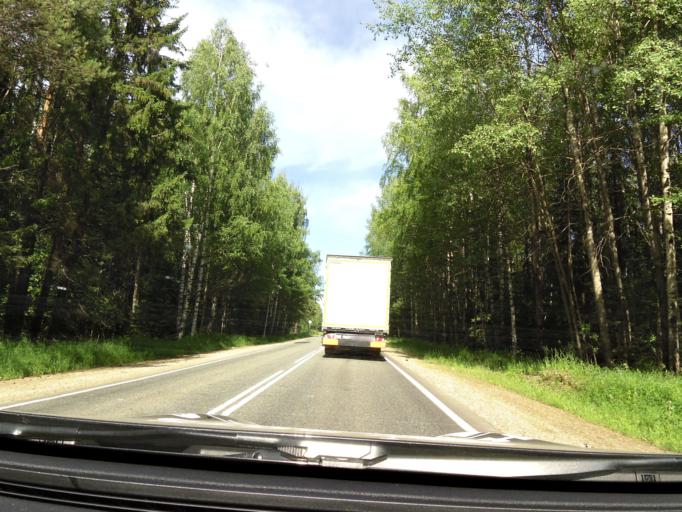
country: RU
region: Kirov
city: Belaya Kholunitsa
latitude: 58.8253
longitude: 50.6238
